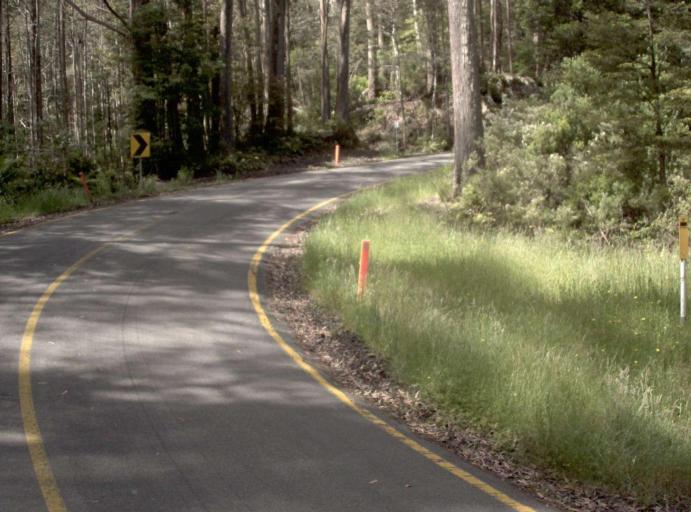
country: AU
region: Victoria
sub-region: Latrobe
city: Moe
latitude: -37.8449
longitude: 146.2478
